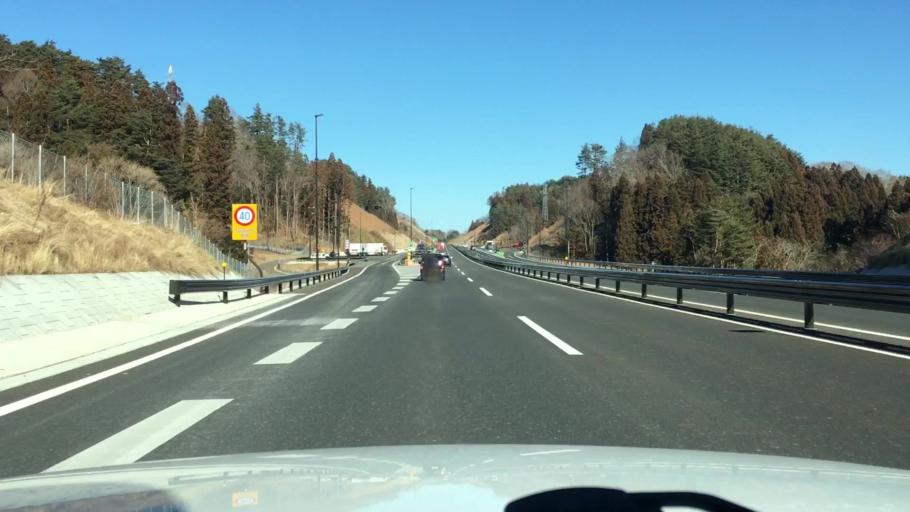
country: JP
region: Iwate
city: Miyako
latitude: 39.5819
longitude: 141.9327
